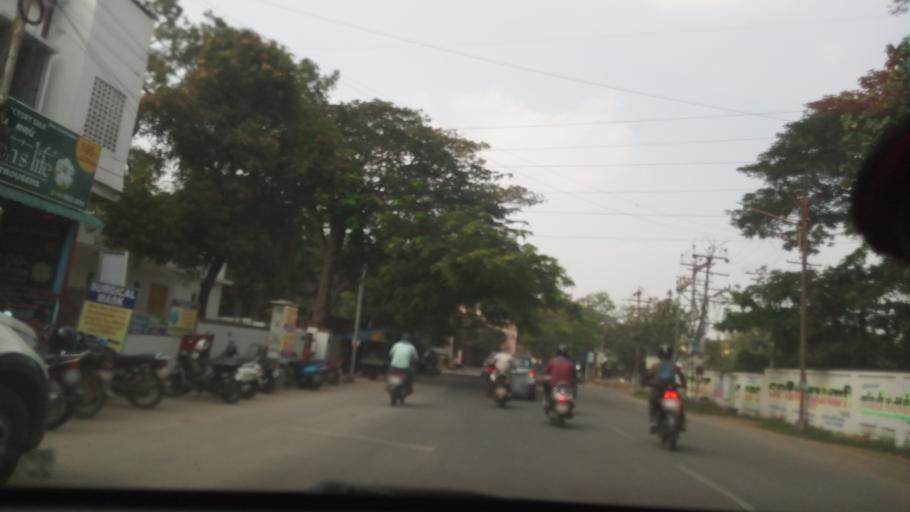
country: IN
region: Tamil Nadu
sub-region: Coimbatore
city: Coimbatore
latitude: 11.0183
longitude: 76.9581
